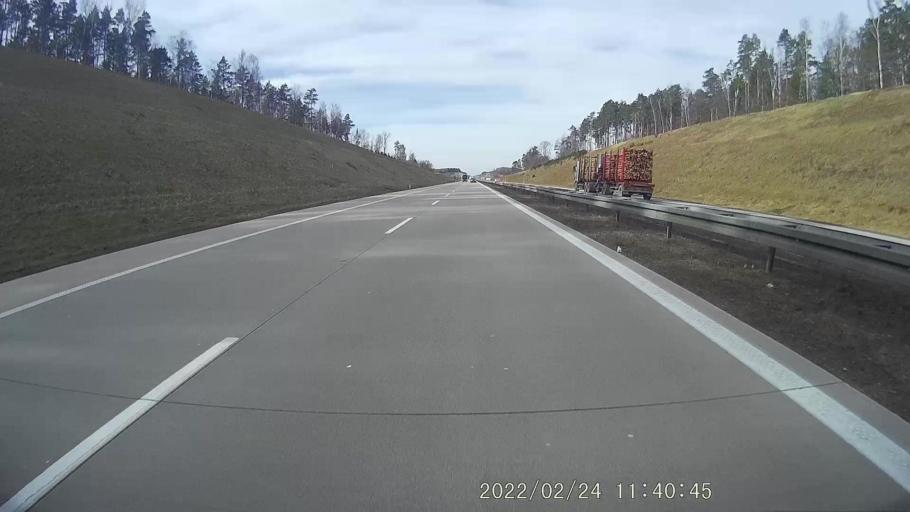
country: PL
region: Lower Silesian Voivodeship
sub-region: Powiat polkowicki
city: Radwanice
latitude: 51.5411
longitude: 15.8830
